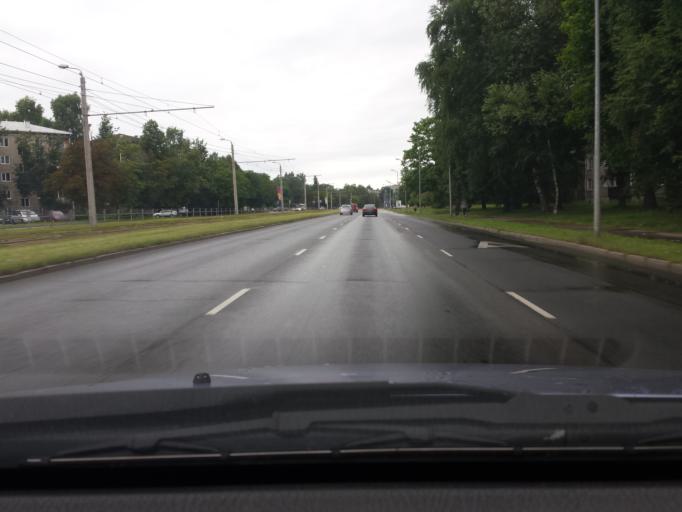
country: LV
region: Kekava
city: Balozi
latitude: 56.9108
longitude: 24.1793
